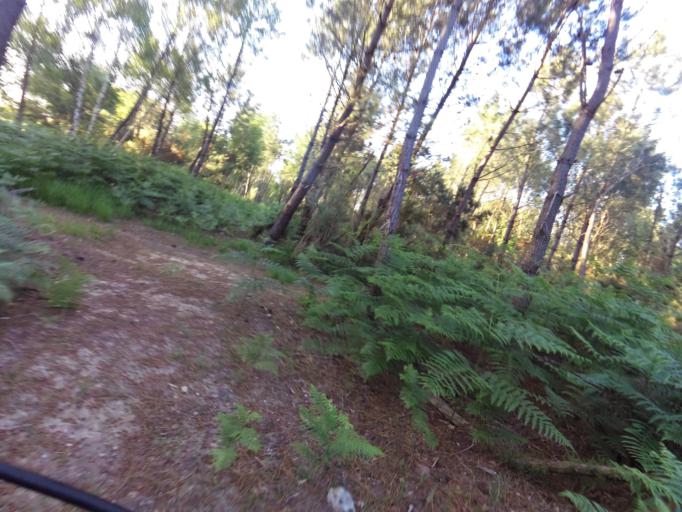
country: FR
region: Brittany
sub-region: Departement du Morbihan
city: Molac
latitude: 47.7432
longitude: -2.4172
